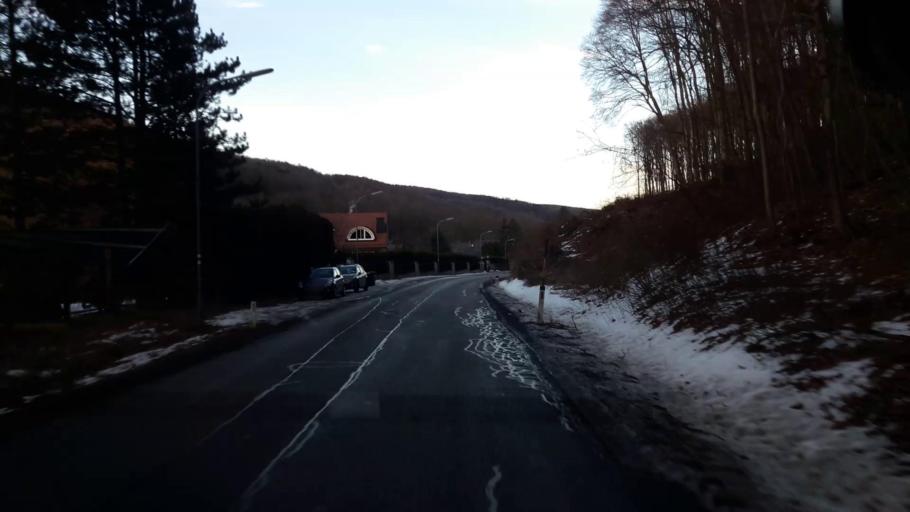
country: AT
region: Lower Austria
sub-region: Politischer Bezirk Wien-Umgebung
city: Klosterneuburg
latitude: 48.2680
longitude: 16.2726
